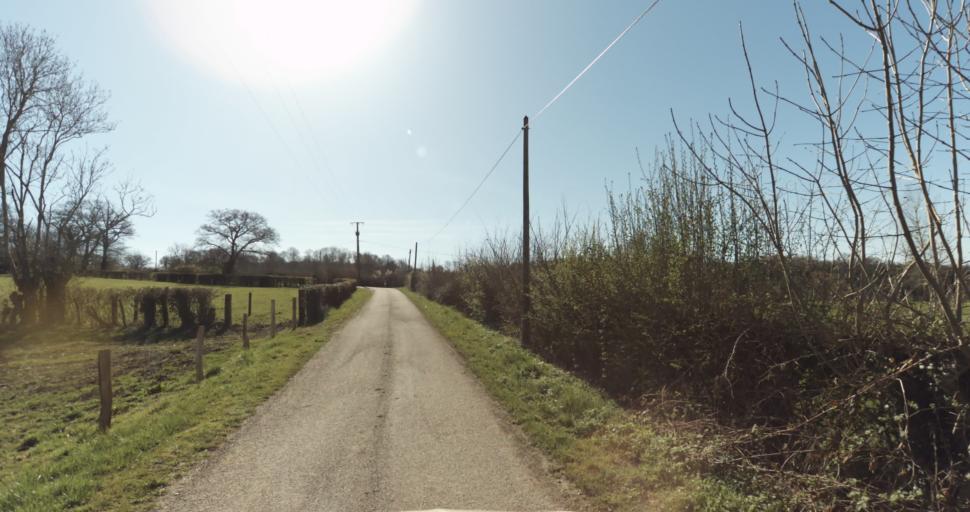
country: FR
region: Lower Normandy
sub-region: Departement de l'Orne
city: Trun
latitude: 48.9197
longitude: 0.0586
